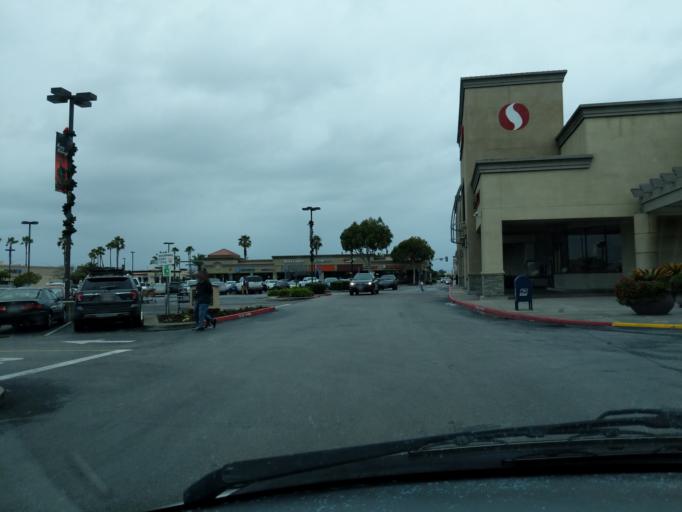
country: US
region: California
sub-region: Monterey County
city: Boronda
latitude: 36.7121
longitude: -121.6525
